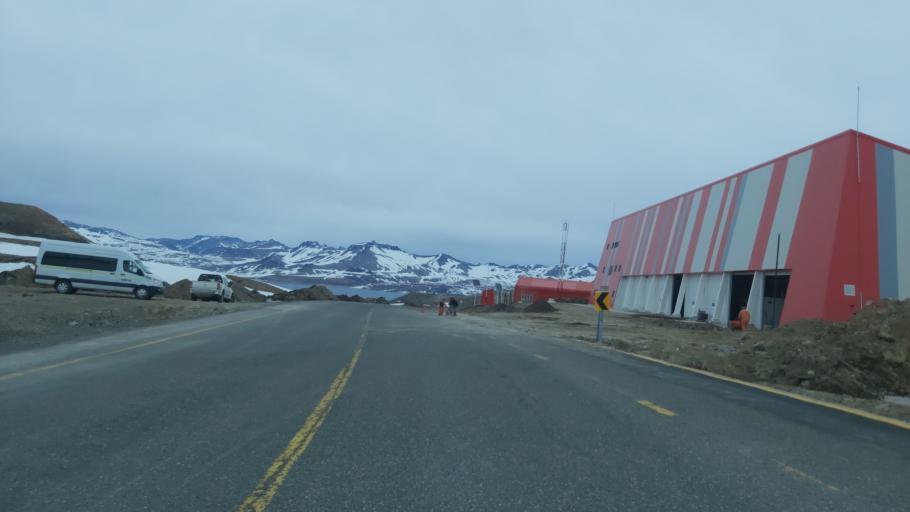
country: CL
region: Maule
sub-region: Provincia de Linares
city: Colbun
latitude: -36.0092
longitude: -70.4819
